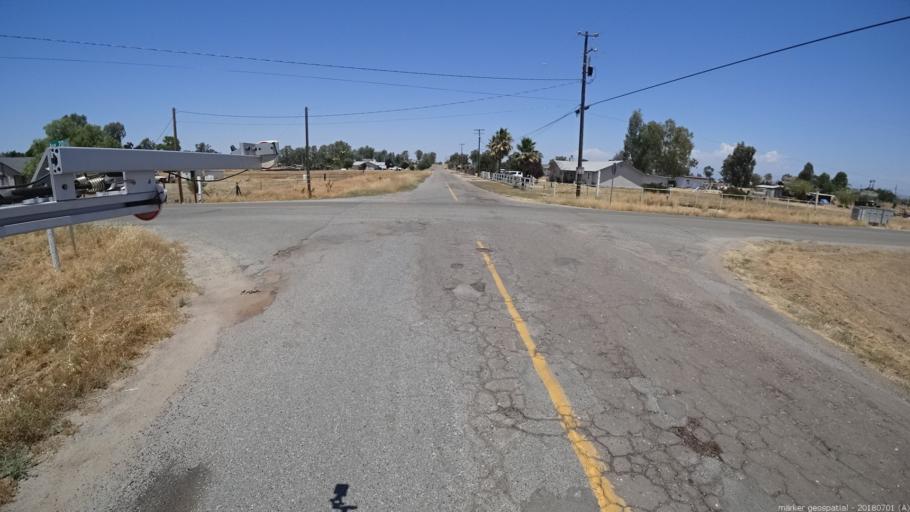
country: US
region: California
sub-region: Madera County
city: Madera Acres
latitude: 37.0467
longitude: -119.9897
